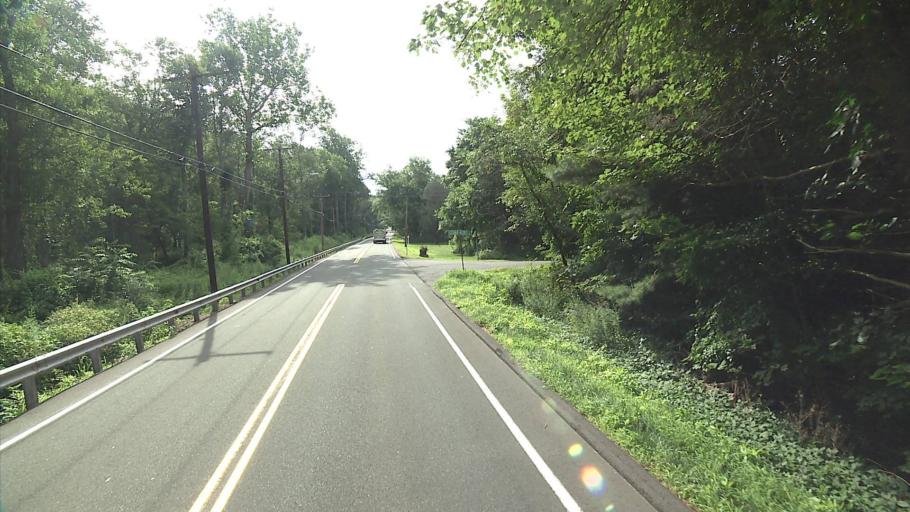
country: US
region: Connecticut
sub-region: New Haven County
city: Woodbridge
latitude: 41.3460
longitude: -73.0202
